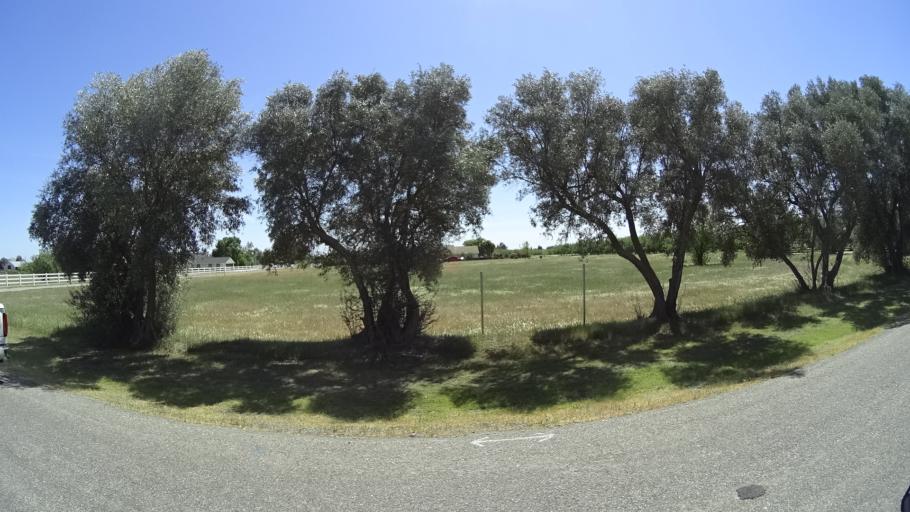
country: US
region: California
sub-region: Glenn County
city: Orland
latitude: 39.7416
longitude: -122.1623
